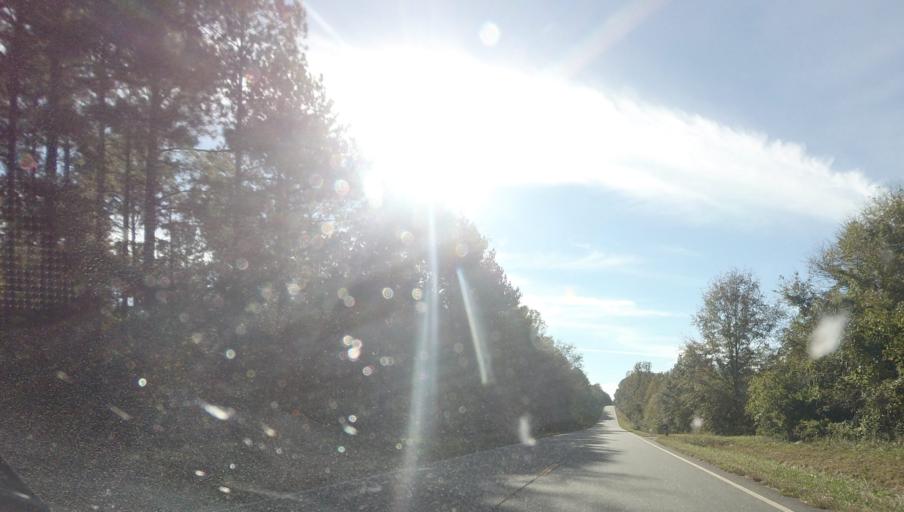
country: US
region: Georgia
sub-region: Talbot County
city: Talbotton
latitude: 32.6934
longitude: -84.4601
